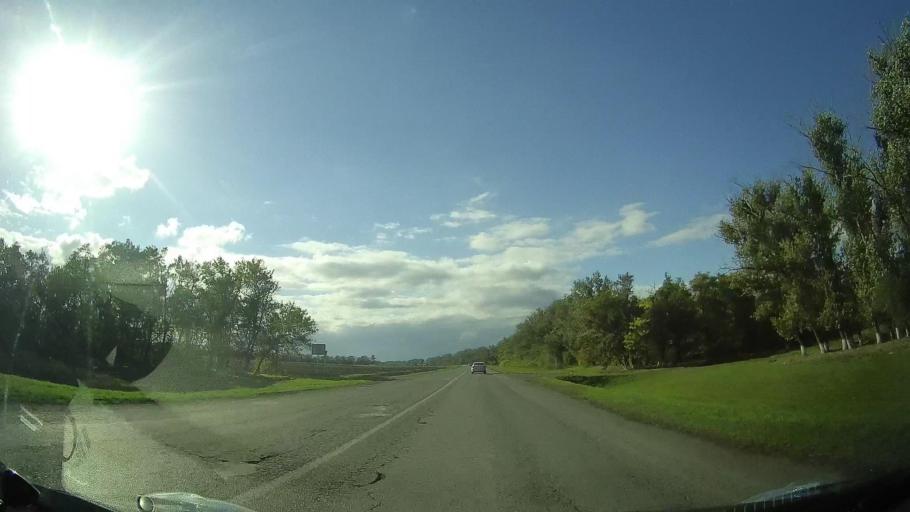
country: RU
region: Rostov
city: Tselina
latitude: 46.5330
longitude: 40.9912
